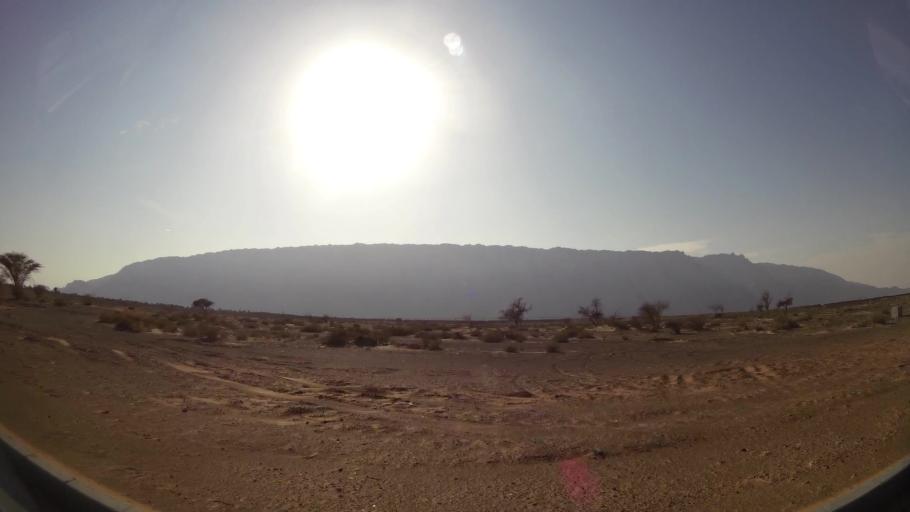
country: AE
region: Abu Dhabi
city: Al Ain
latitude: 24.0350
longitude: 55.8387
